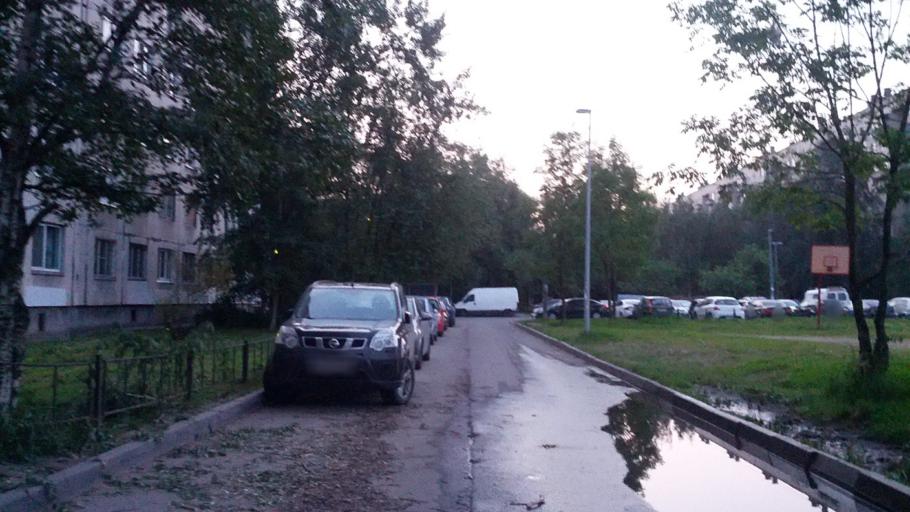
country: RU
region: St.-Petersburg
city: Obukhovo
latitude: 59.9040
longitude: 30.4641
